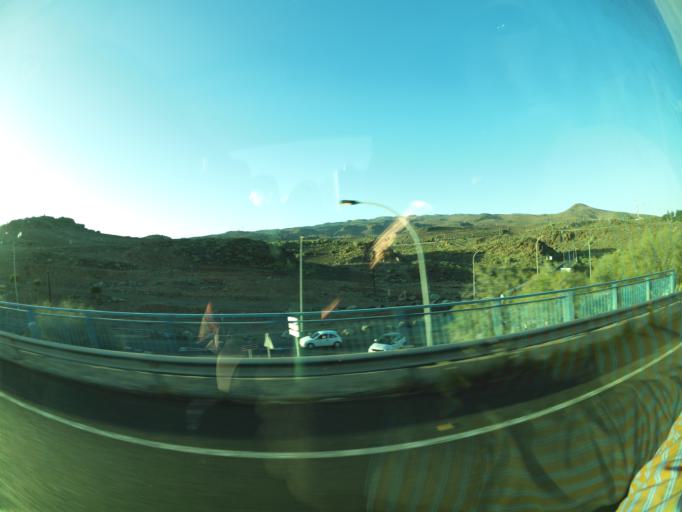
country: ES
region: Canary Islands
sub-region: Provincia de Las Palmas
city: Playa del Ingles
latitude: 27.7774
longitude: -15.5288
